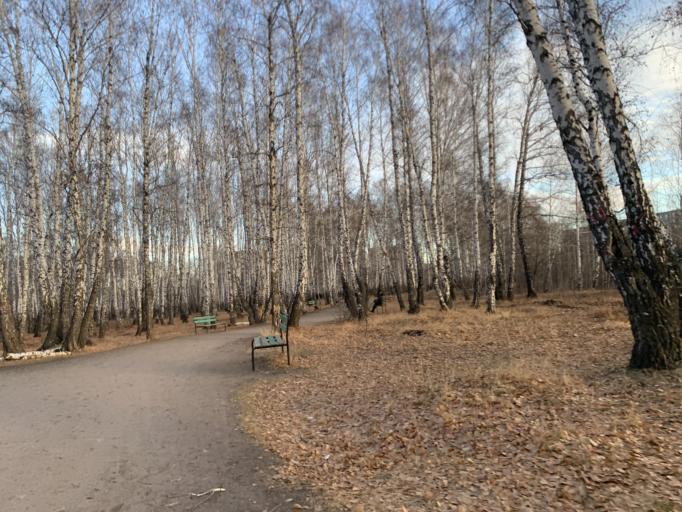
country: RU
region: Chelyabinsk
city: Roshchino
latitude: 55.2007
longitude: 61.3080
